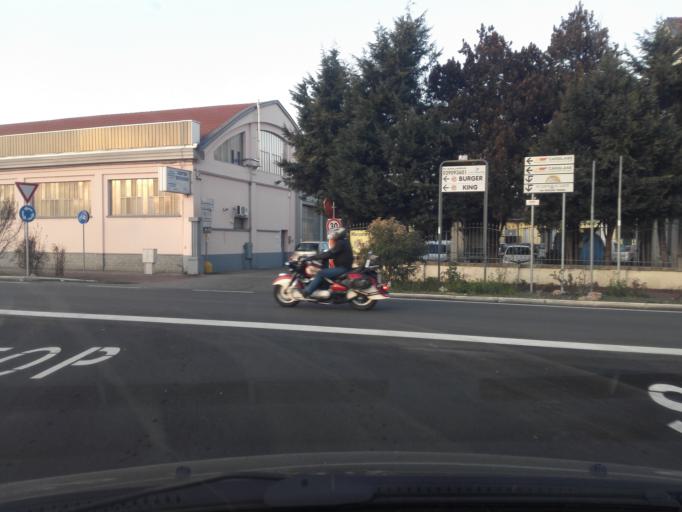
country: IT
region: Piedmont
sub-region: Provincia di Alessandria
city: Alessandria
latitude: 44.9174
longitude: 8.6014
